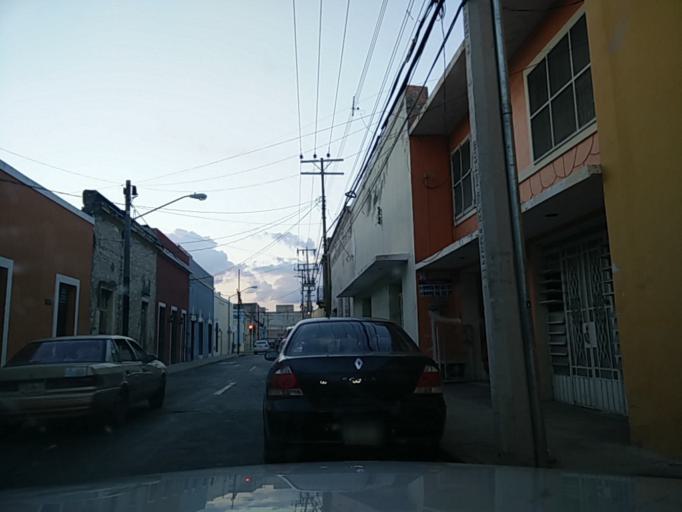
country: MX
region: Yucatan
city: Merida
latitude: 20.9706
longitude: -89.6272
